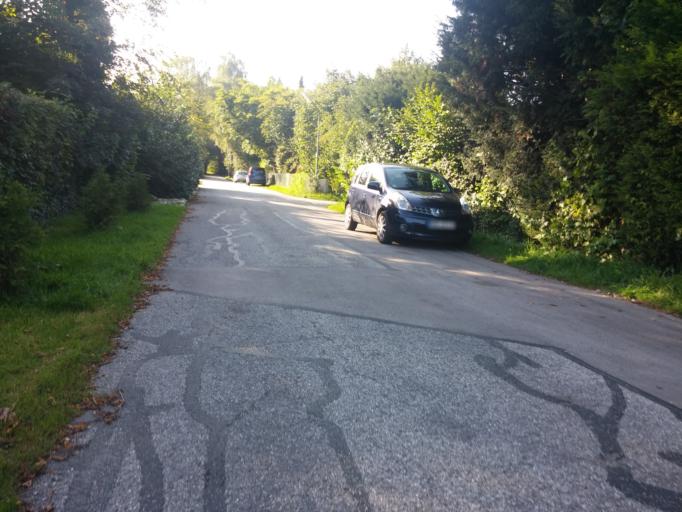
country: DE
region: Bavaria
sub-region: Upper Bavaria
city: Kirchseeon
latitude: 48.0826
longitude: 11.8696
